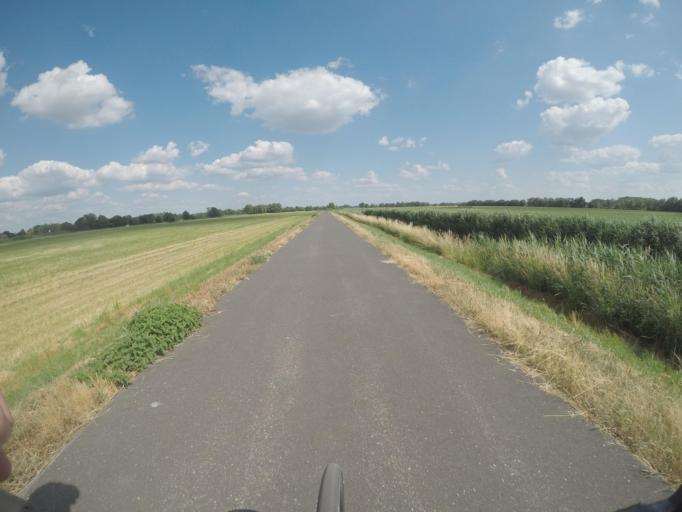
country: DE
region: Brandenburg
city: Ketzin
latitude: 52.4697
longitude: 12.8294
